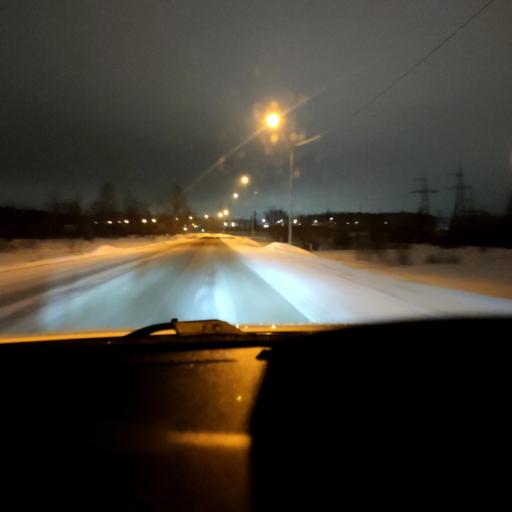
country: RU
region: Tatarstan
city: Vysokaya Gora
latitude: 55.8865
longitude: 49.2387
